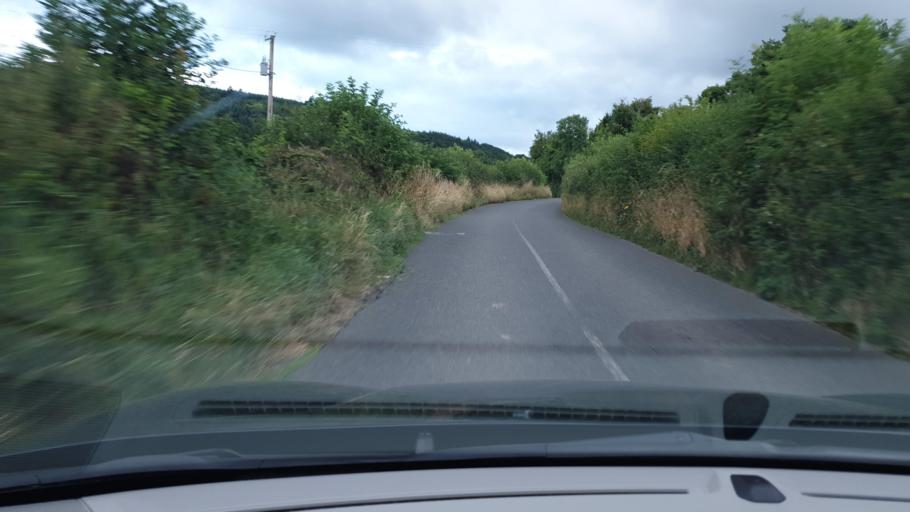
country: IE
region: Leinster
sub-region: South Dublin
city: Saggart
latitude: 53.2693
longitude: -6.4477
